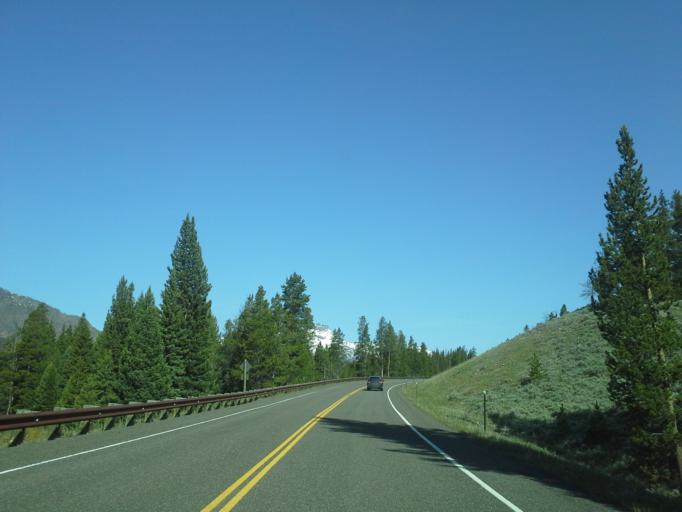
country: US
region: Montana
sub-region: Carbon County
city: Red Lodge
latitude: 44.9374
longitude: -109.7652
